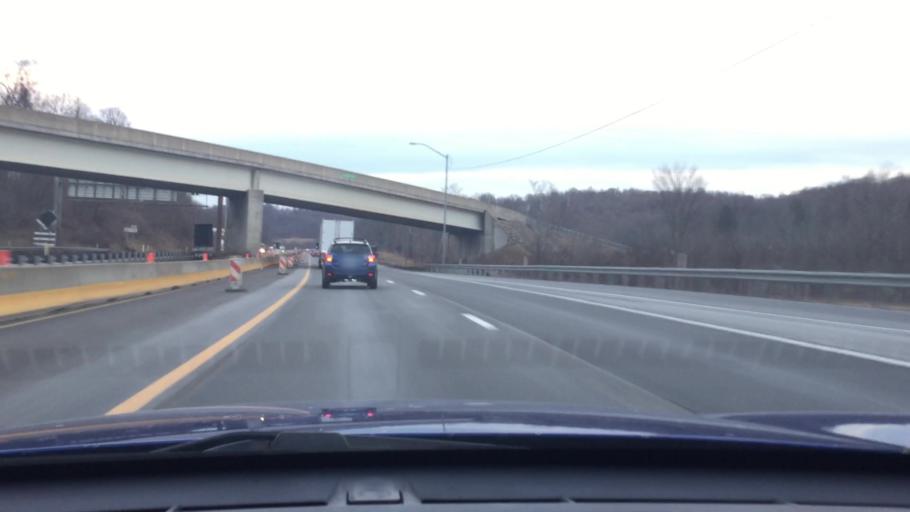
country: US
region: Pennsylvania
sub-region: Washington County
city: East Washington
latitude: 40.1624
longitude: -80.1888
